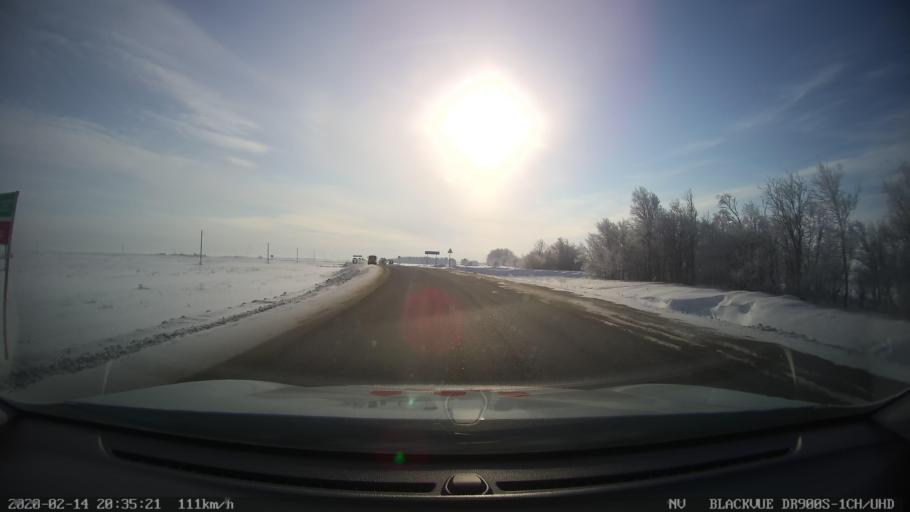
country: RU
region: Tatarstan
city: Kuybyshevskiy Zaton
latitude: 55.3835
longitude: 48.9823
